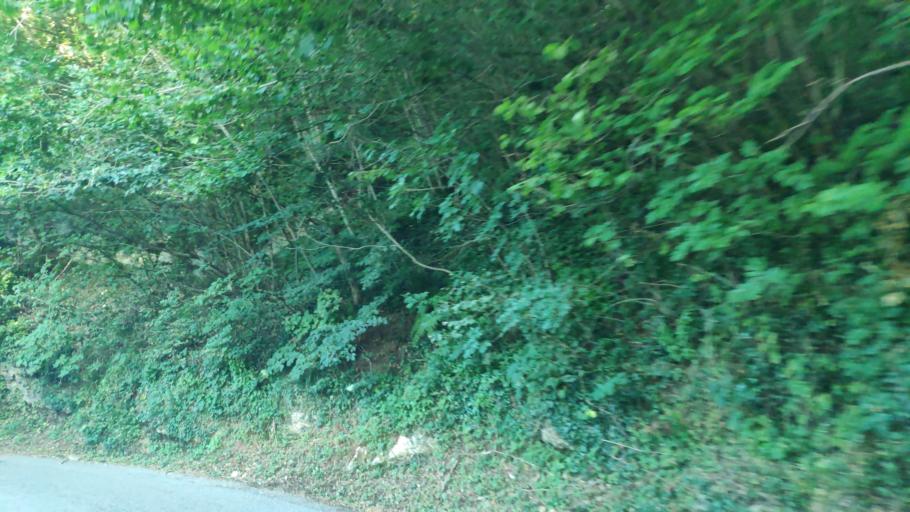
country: IT
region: Campania
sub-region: Provincia di Salerno
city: Pietre
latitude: 40.7179
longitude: 14.6142
